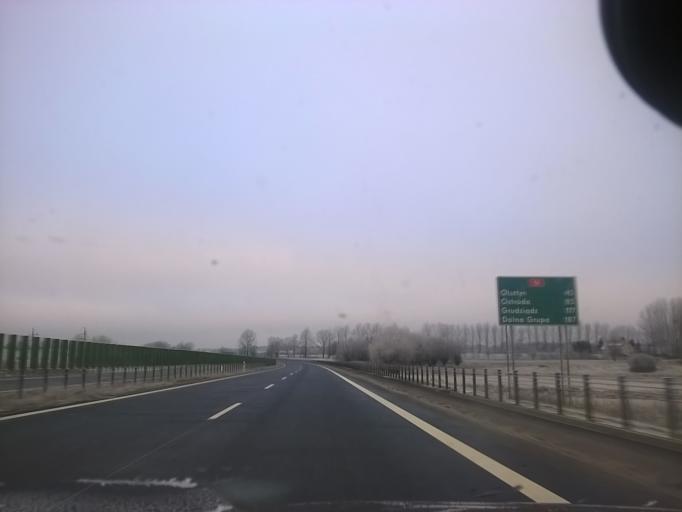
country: PL
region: Warmian-Masurian Voivodeship
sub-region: Powiat olsztynski
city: Biskupiec
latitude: 53.8322
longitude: 21.0551
